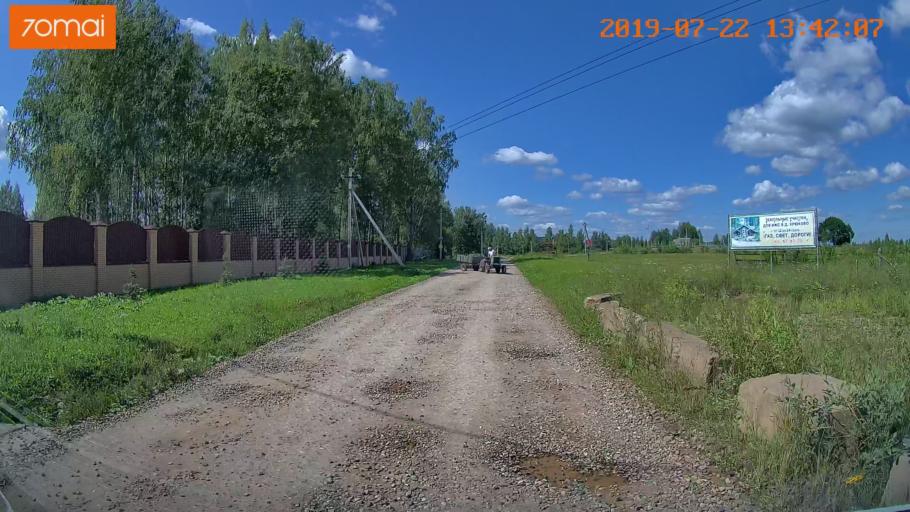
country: RU
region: Ivanovo
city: Novo-Talitsy
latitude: 57.0810
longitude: 40.8755
